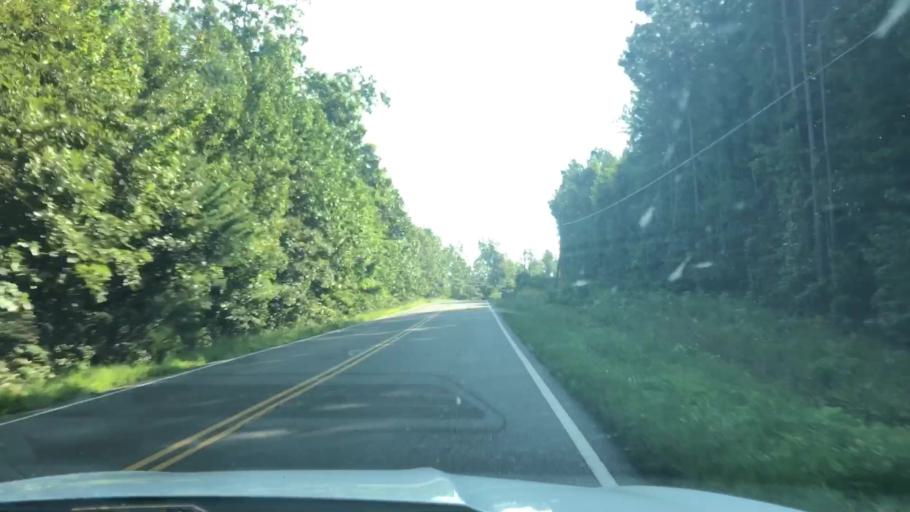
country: US
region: Virginia
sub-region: Richmond County
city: Warsaw
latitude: 37.8941
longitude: -76.6539
